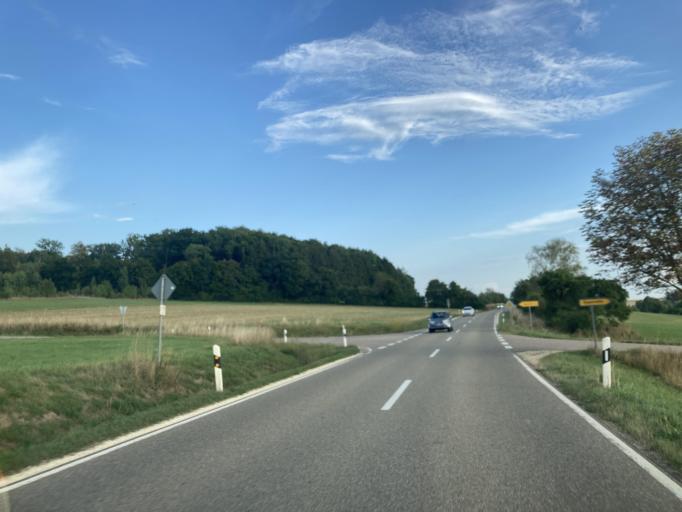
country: DE
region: Baden-Wuerttemberg
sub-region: Regierungsbezirk Stuttgart
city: Dischingen
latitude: 48.6804
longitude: 10.3727
